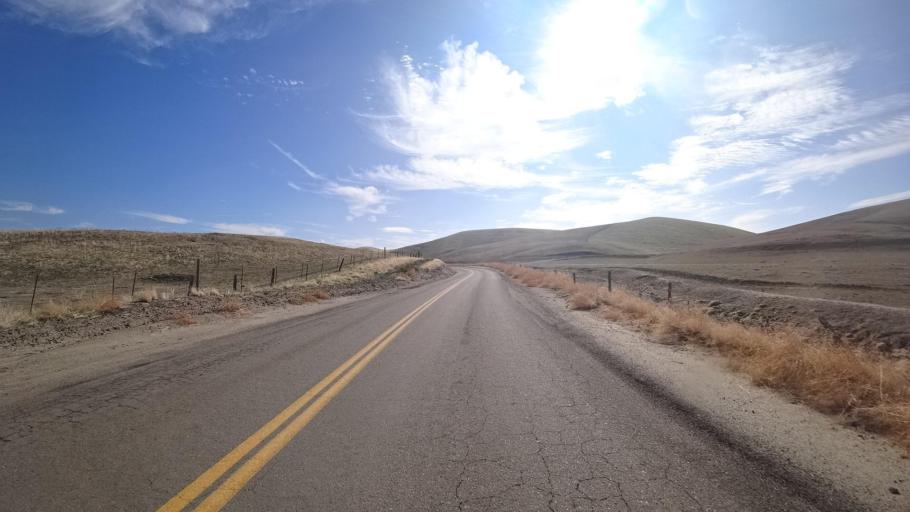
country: US
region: California
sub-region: Kern County
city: Oildale
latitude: 35.6289
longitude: -118.9437
